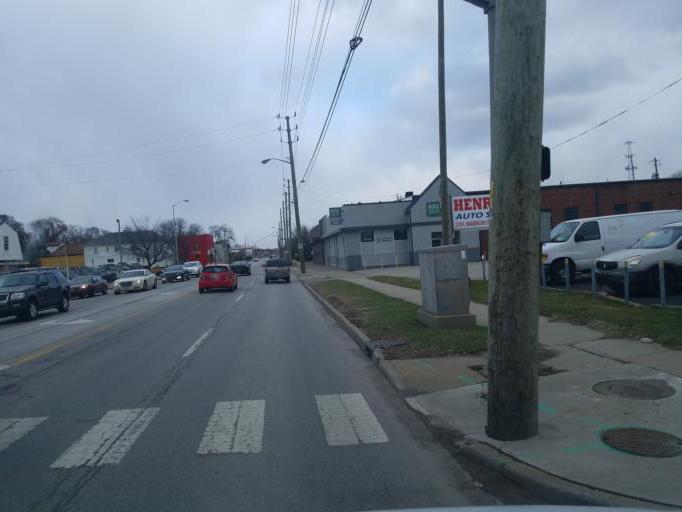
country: US
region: Indiana
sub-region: Marion County
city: Indianapolis
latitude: 39.7679
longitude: -86.1218
